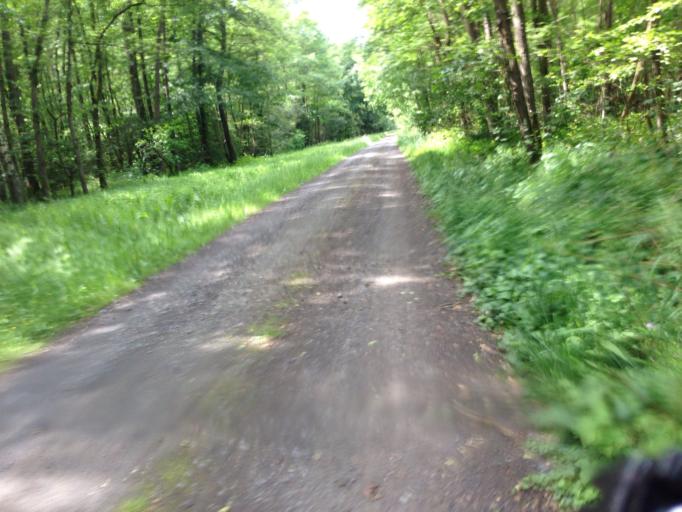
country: DE
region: Hesse
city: Bruchkobel
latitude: 50.1715
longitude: 8.9464
